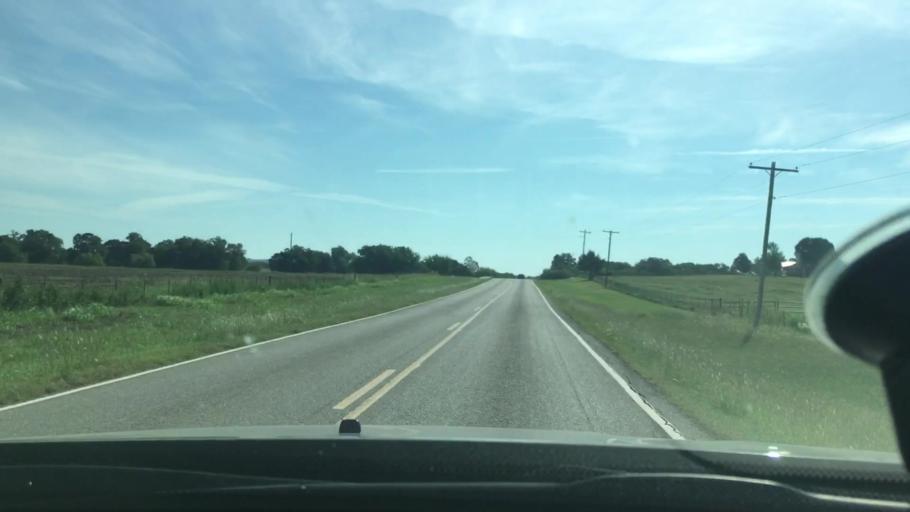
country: US
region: Oklahoma
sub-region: Carter County
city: Ardmore
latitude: 34.3327
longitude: -97.1757
